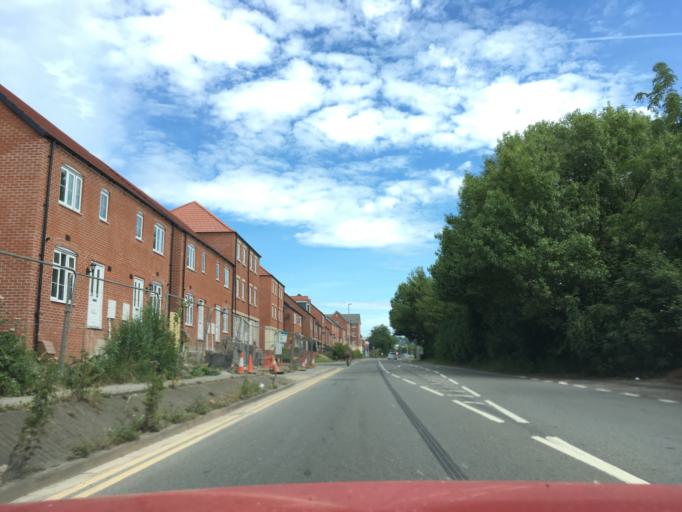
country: GB
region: Wales
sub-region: Newport
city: Newport
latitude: 51.5743
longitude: -2.9691
